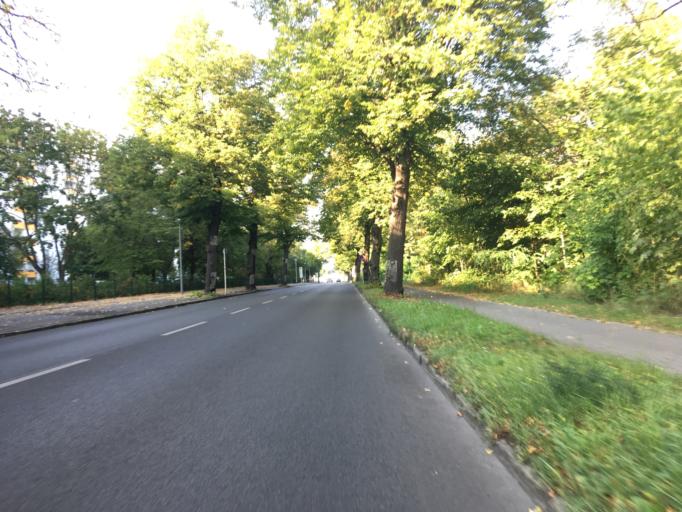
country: DE
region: Berlin
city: Berlin Koepenick
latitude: 52.4430
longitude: 13.5935
